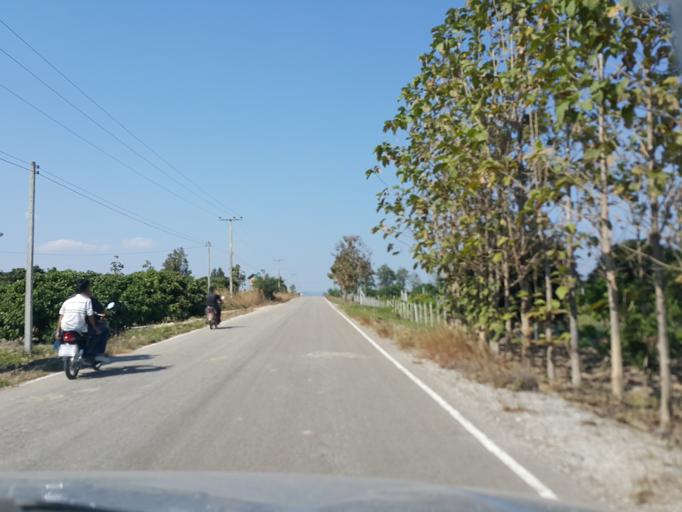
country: TH
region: Chiang Mai
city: Mae Wang
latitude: 18.5582
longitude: 98.7944
